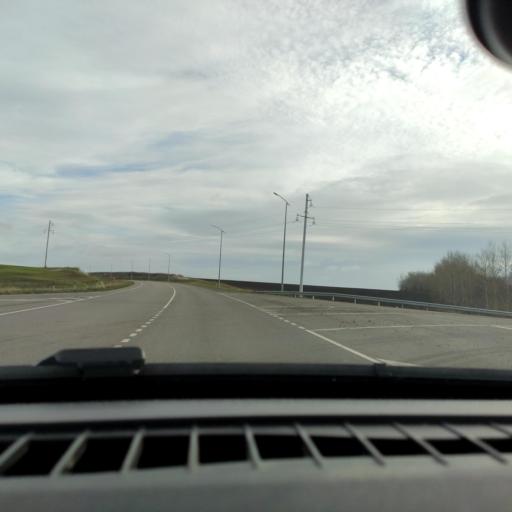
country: RU
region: Belgorod
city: Ilovka
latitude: 50.6719
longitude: 38.6323
